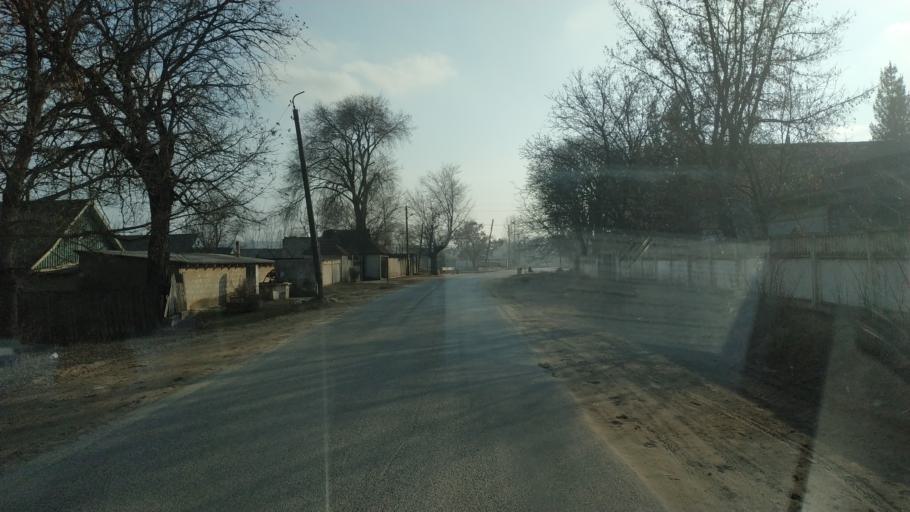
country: MD
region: Hincesti
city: Dancu
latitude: 46.7786
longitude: 28.3482
